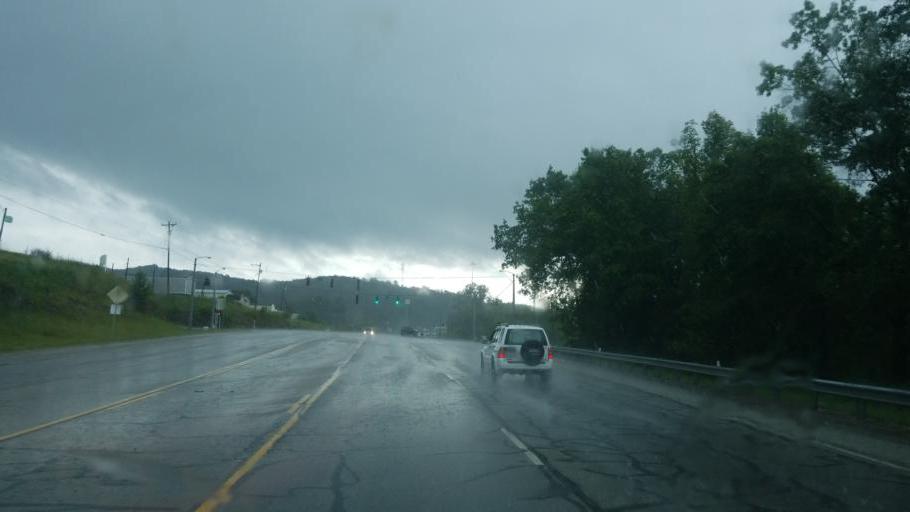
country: US
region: Kentucky
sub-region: Rowan County
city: Morehead
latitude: 38.1951
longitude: -83.4814
